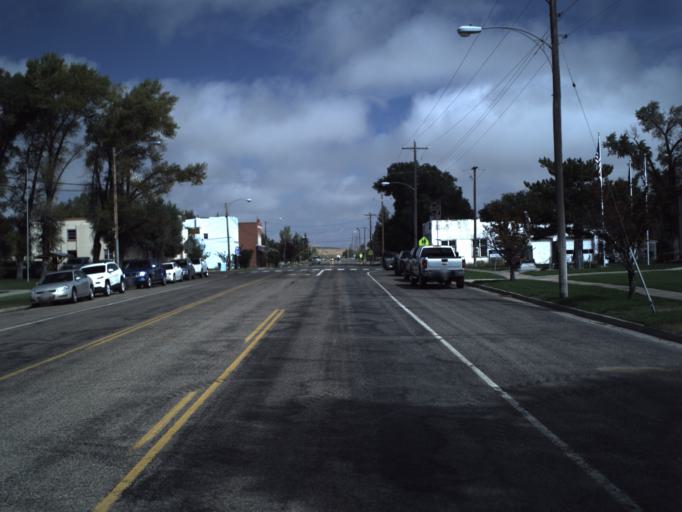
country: US
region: Utah
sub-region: Rich County
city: Randolph
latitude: 41.6646
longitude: -111.1849
